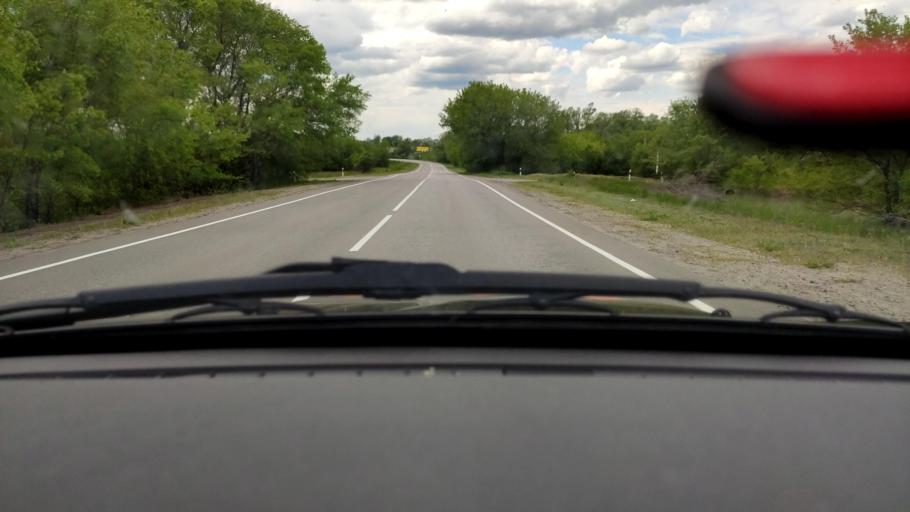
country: RU
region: Voronezj
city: Ostrogozhsk
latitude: 51.0549
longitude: 38.9258
